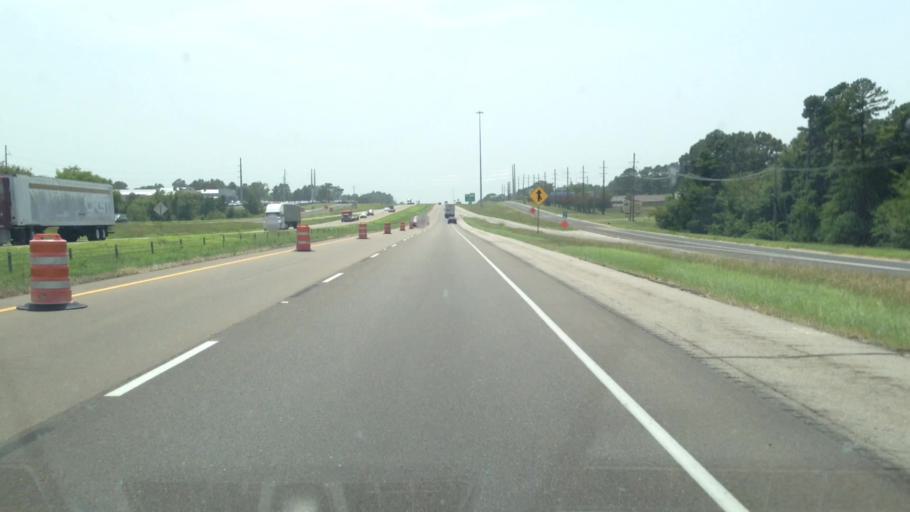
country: US
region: Texas
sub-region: Titus County
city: Mount Pleasant
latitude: 33.1778
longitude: -94.9740
